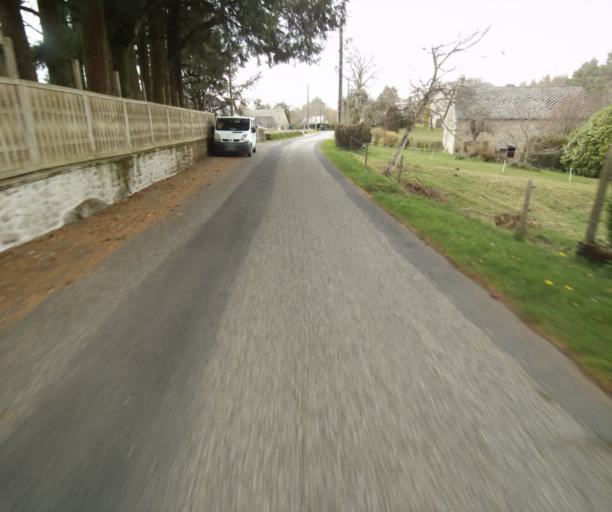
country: FR
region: Limousin
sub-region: Departement de la Correze
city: Correze
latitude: 45.2825
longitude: 1.9717
